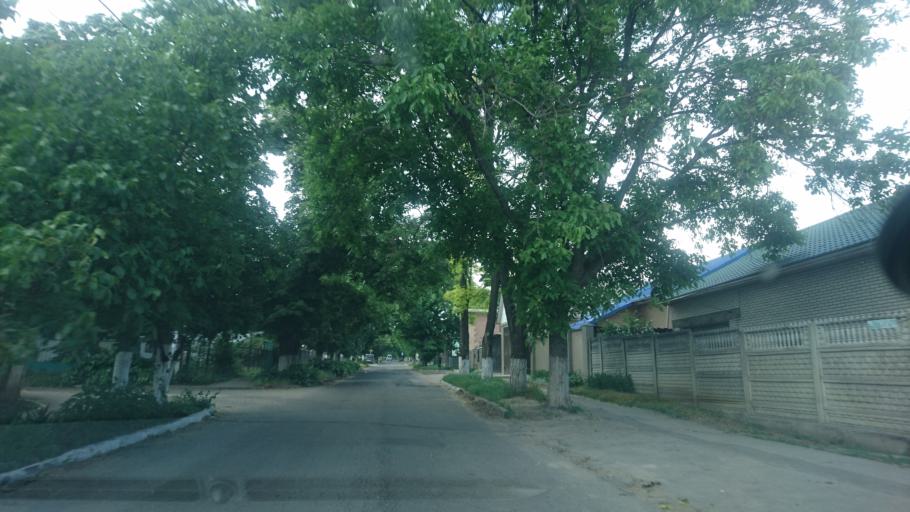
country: MD
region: Chisinau
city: Chisinau
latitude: 47.0480
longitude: 28.8468
